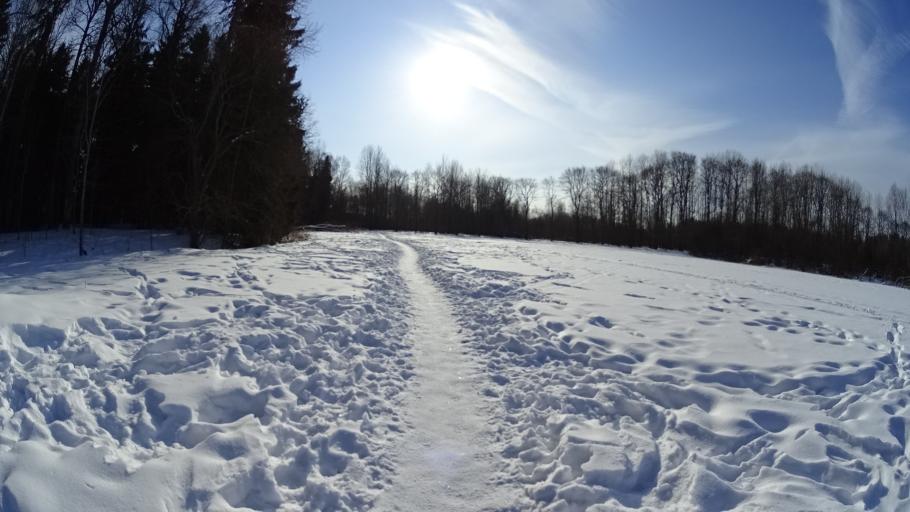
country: FI
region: Uusimaa
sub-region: Helsinki
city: Kauniainen
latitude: 60.2450
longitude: 24.7291
